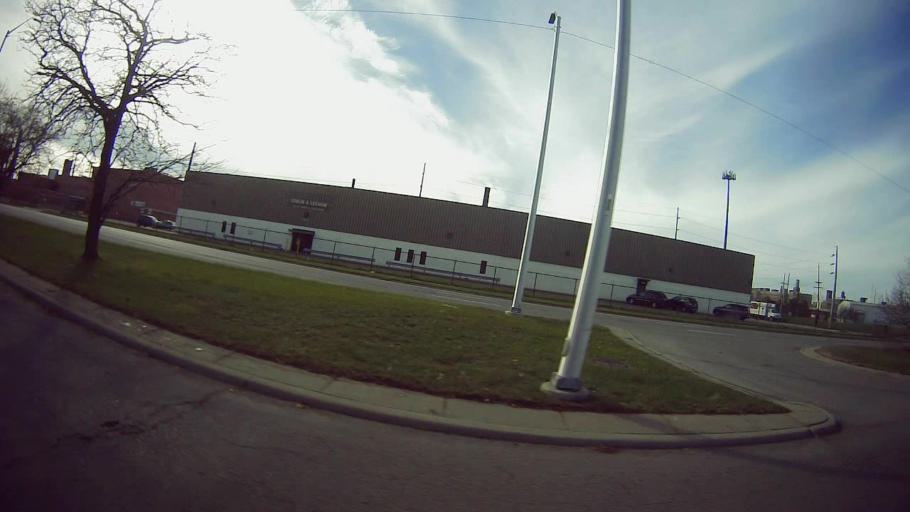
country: US
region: Michigan
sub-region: Wayne County
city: Hamtramck
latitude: 42.3759
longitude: -83.0520
